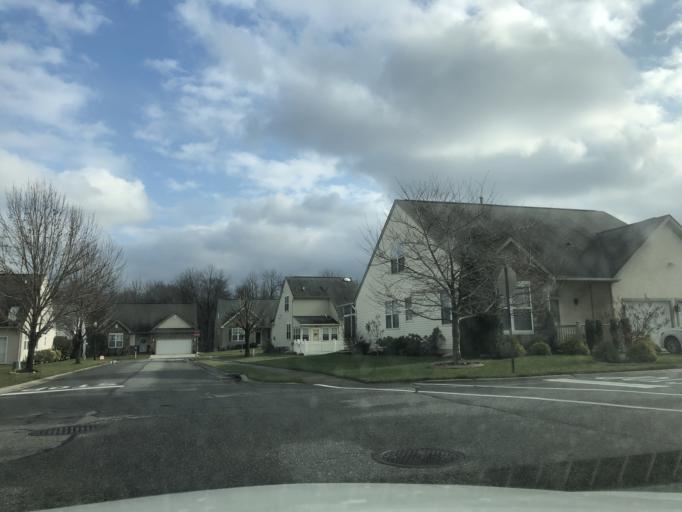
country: US
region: New Jersey
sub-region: Camden County
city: Glendora
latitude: 39.8415
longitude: -75.0999
